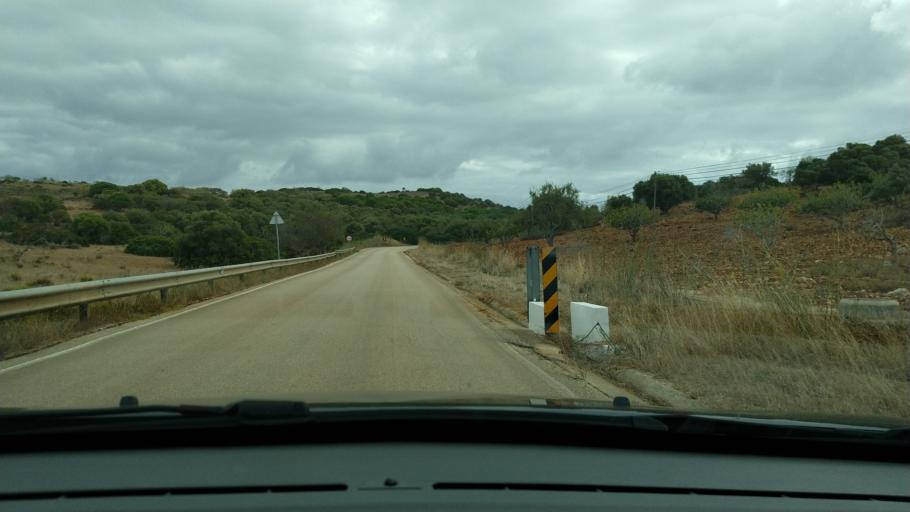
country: PT
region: Faro
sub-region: Lagos
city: Lagos
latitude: 37.0849
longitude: -8.7779
